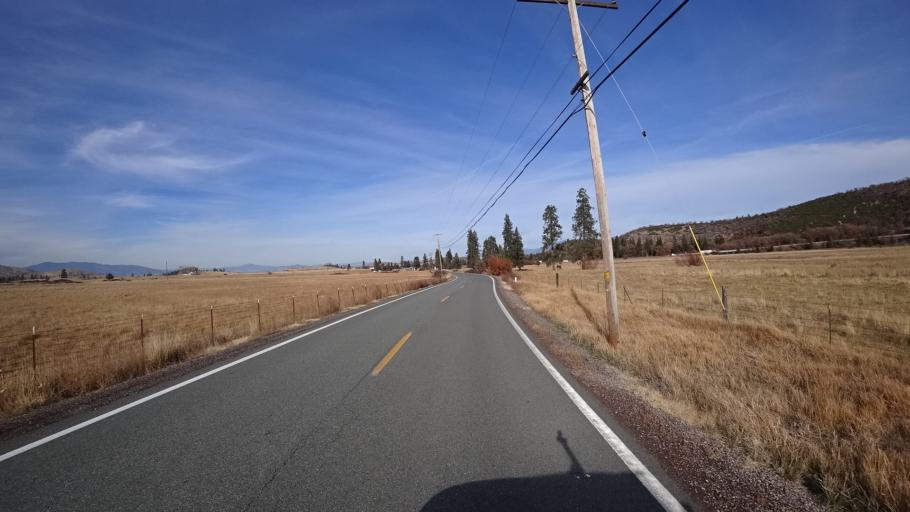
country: US
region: California
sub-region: Siskiyou County
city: Weed
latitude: 41.4342
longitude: -122.4364
